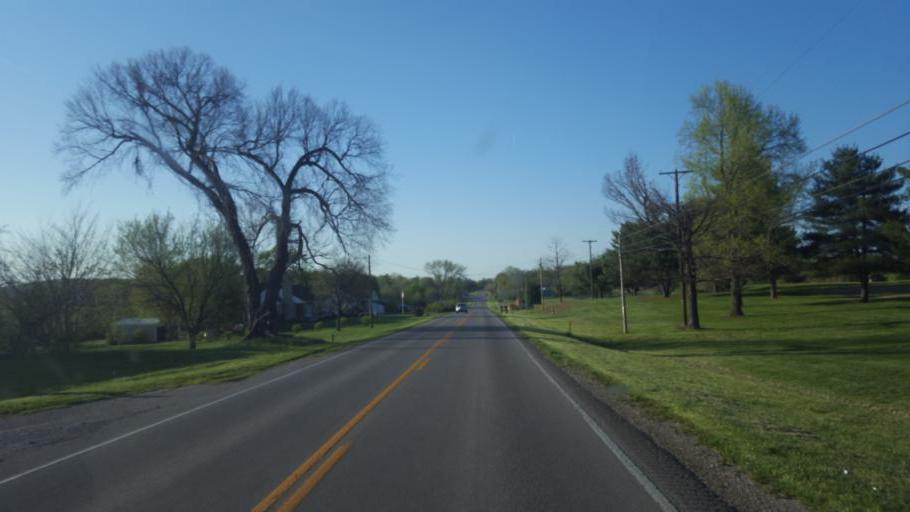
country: US
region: Kentucky
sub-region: Hart County
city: Munfordville
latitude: 37.2328
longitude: -85.8907
